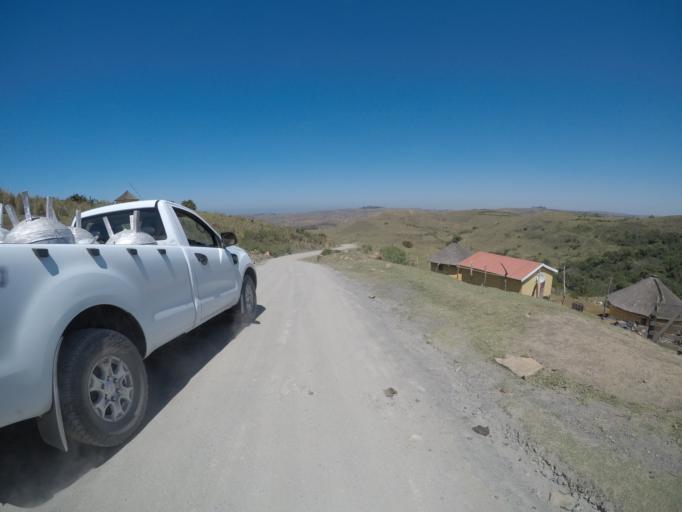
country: ZA
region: Eastern Cape
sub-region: OR Tambo District Municipality
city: Libode
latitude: -32.0104
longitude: 29.0732
